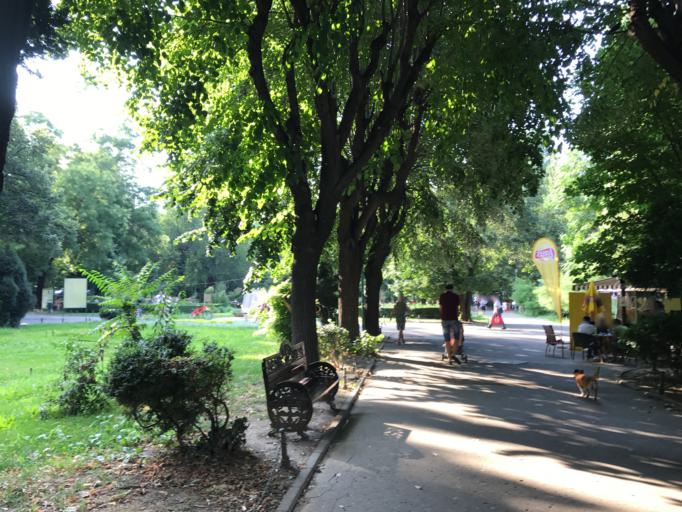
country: RO
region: Bucuresti
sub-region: Municipiul Bucuresti
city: Bucuresti
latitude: 44.4381
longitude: 26.0887
